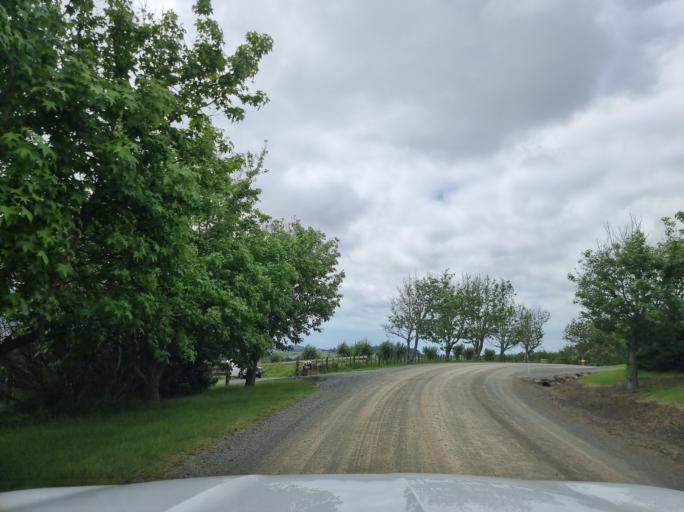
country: NZ
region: Auckland
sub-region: Auckland
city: Wellsford
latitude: -36.0933
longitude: 174.5314
